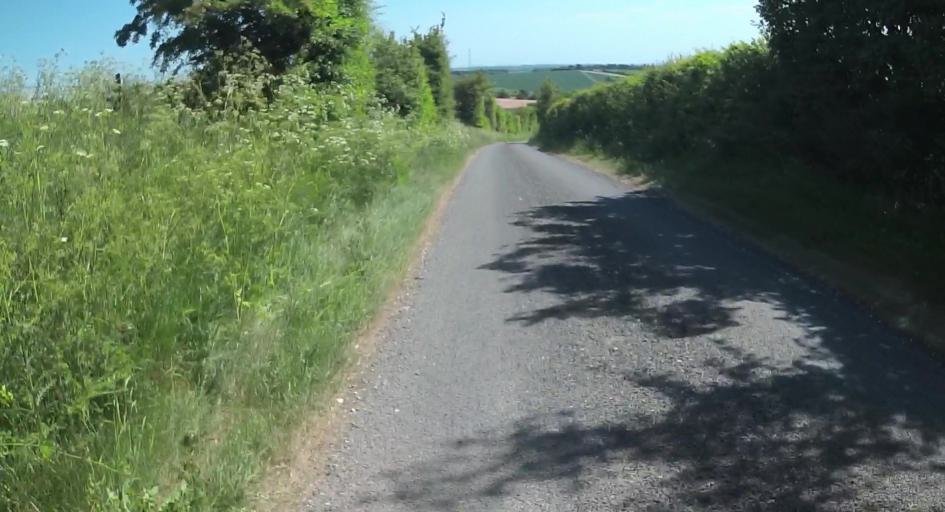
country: GB
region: England
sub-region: Hampshire
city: Kingsclere
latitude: 51.3023
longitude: -1.2947
